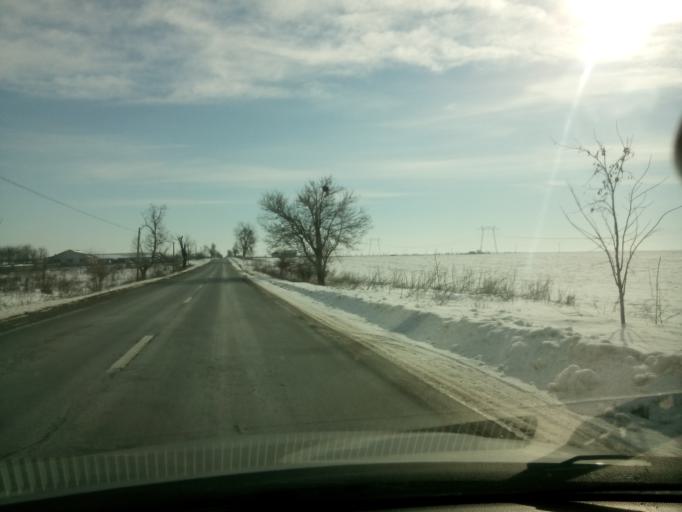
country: RO
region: Calarasi
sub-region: Comuna Frumusani
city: Frumusani
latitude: 44.2678
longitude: 26.3481
